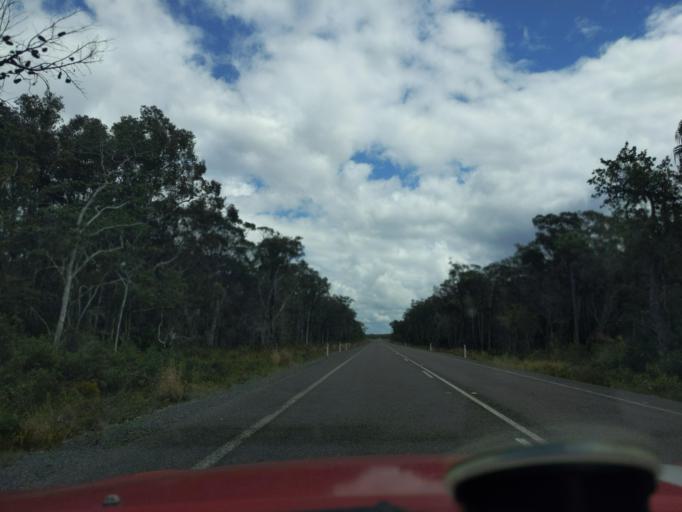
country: AU
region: New South Wales
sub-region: Great Lakes
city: Hawks Nest
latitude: -32.5913
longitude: 152.2654
